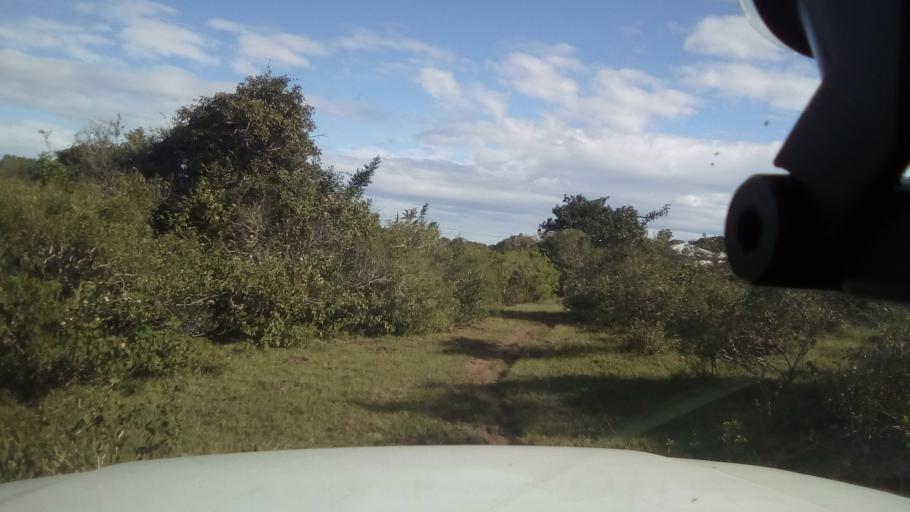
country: ZA
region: Eastern Cape
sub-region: Amathole District Municipality
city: Komga
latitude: -32.7760
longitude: 27.9315
